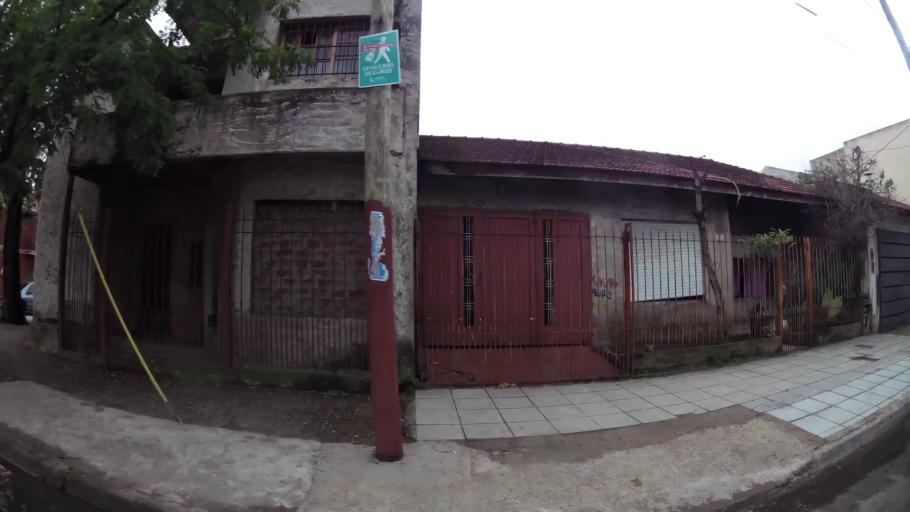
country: AR
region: Buenos Aires
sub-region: Partido de Lomas de Zamora
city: Lomas de Zamora
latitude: -34.7406
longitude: -58.3728
